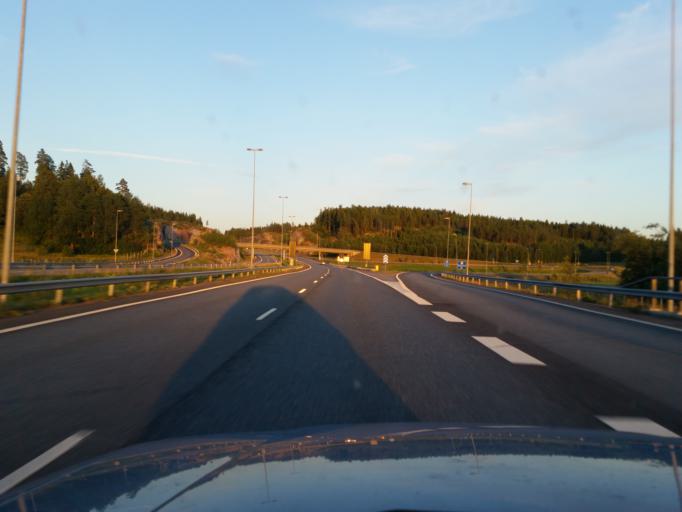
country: FI
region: Varsinais-Suomi
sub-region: Salo
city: Muurla
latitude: 60.3822
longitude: 23.3136
